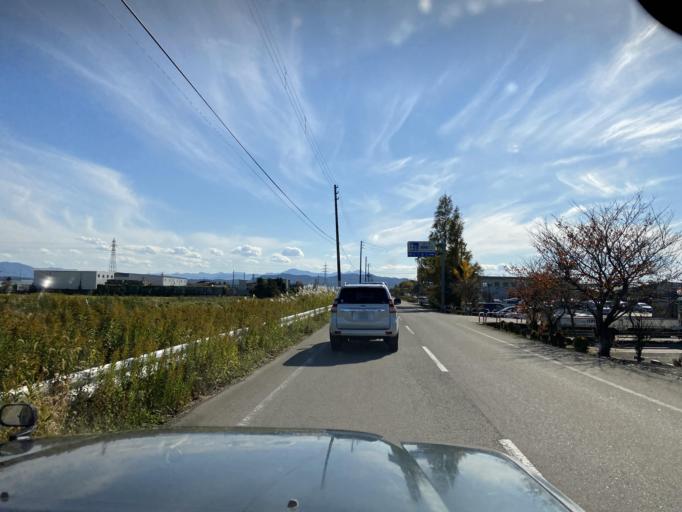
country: JP
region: Niigata
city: Niitsu-honcho
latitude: 37.7937
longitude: 139.0791
